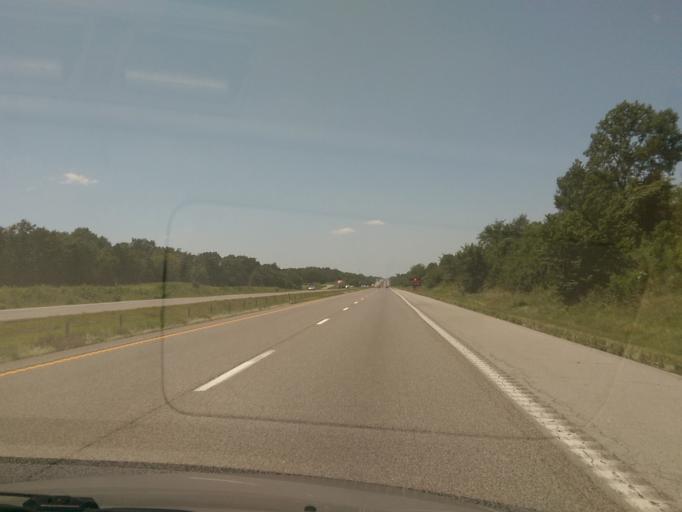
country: US
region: Missouri
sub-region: Saline County
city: Marshall
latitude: 38.9543
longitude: -93.1044
